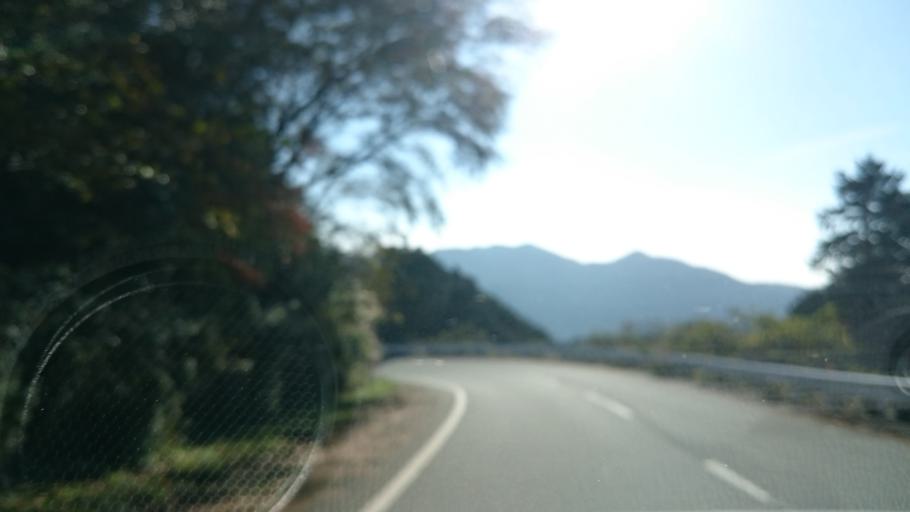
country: JP
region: Shizuoka
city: Heda
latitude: 34.9793
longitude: 138.8136
